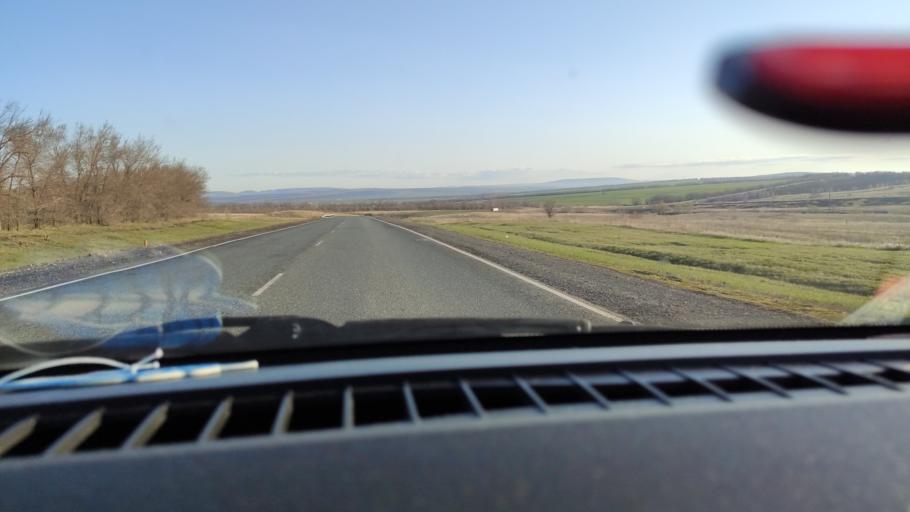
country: RU
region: Saratov
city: Balakovo
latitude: 52.1222
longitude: 47.7532
